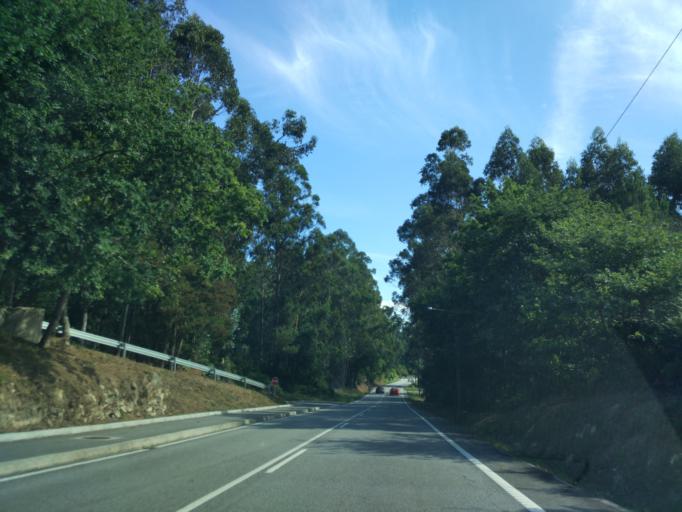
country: ES
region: Galicia
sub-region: Provincia da Coruna
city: Padron
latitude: 42.7215
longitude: -8.6805
